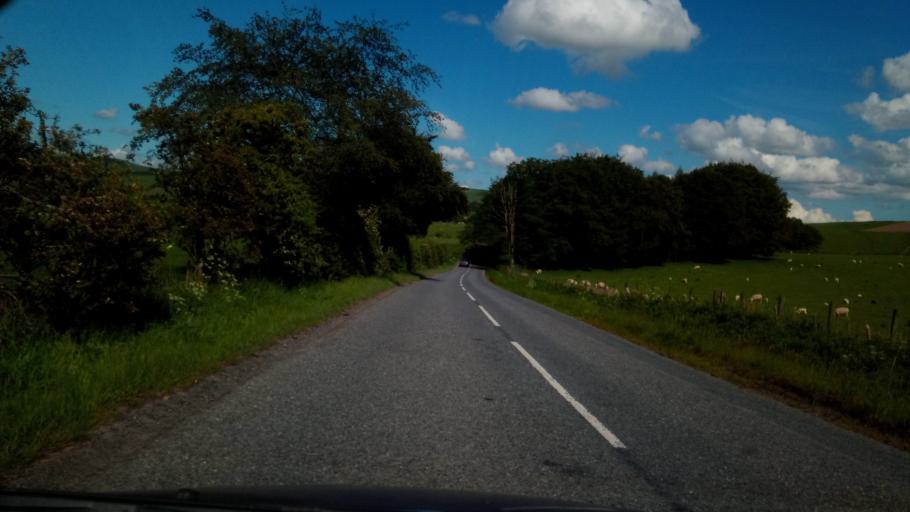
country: GB
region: Scotland
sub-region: The Scottish Borders
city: Jedburgh
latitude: 55.3875
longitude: -2.6341
